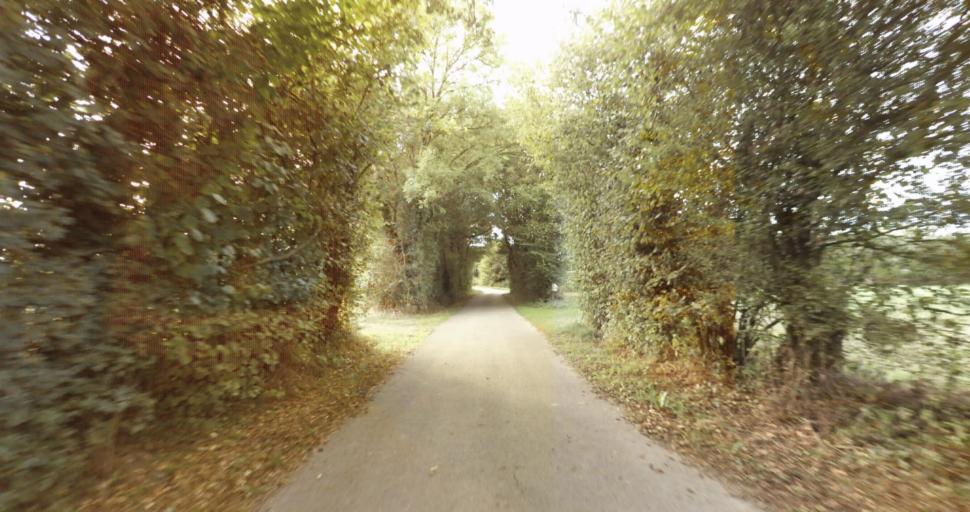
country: FR
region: Lower Normandy
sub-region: Departement de l'Orne
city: Gace
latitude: 48.7491
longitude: 0.2752
